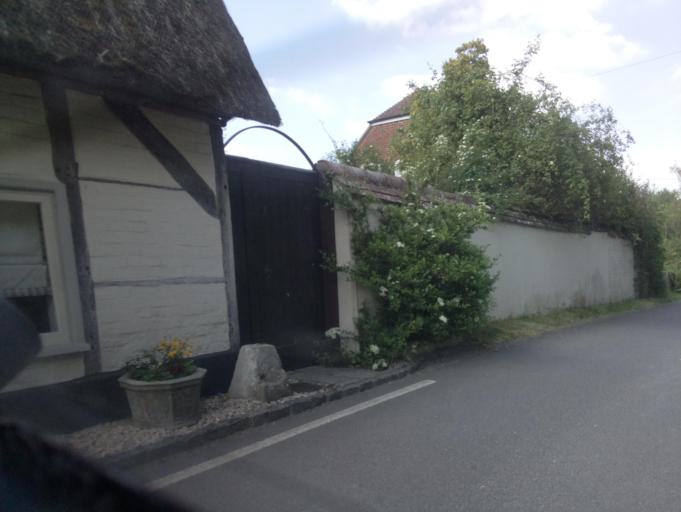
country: GB
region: England
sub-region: Wiltshire
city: Rushall
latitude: 51.2614
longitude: -1.7985
